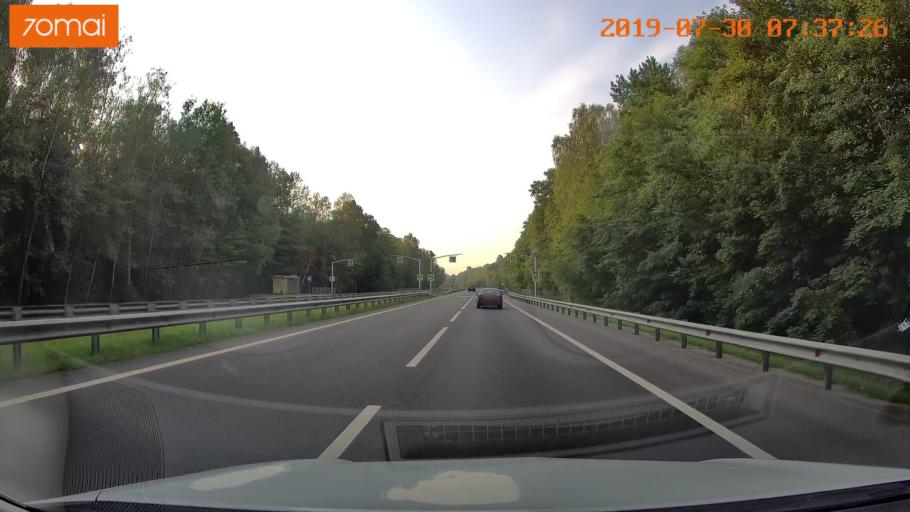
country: RU
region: Kaliningrad
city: Gvardeysk
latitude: 54.6559
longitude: 21.1460
